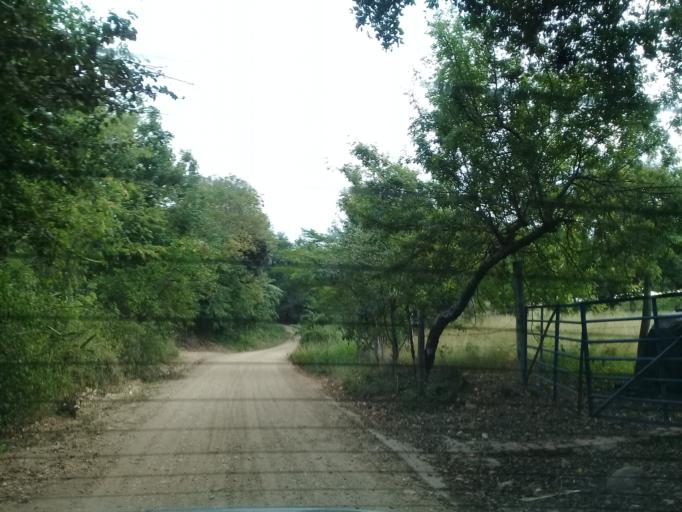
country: CO
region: Cundinamarca
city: Agua de Dios
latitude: 4.3656
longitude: -74.7212
